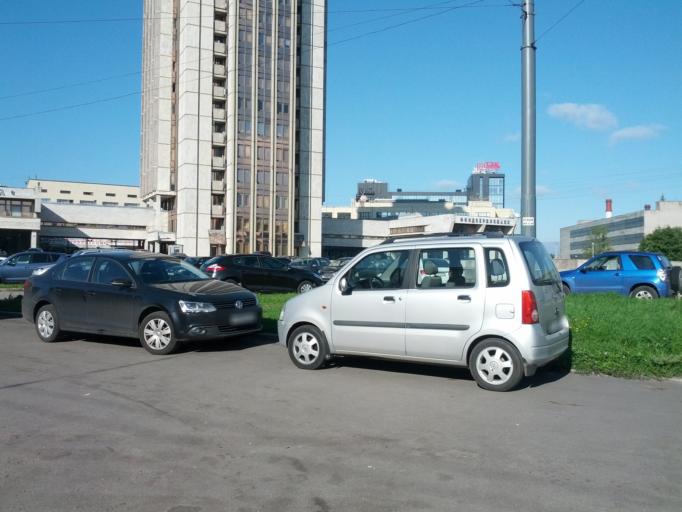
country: RU
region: Leningrad
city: Sampsonievskiy
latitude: 59.9838
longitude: 30.3333
